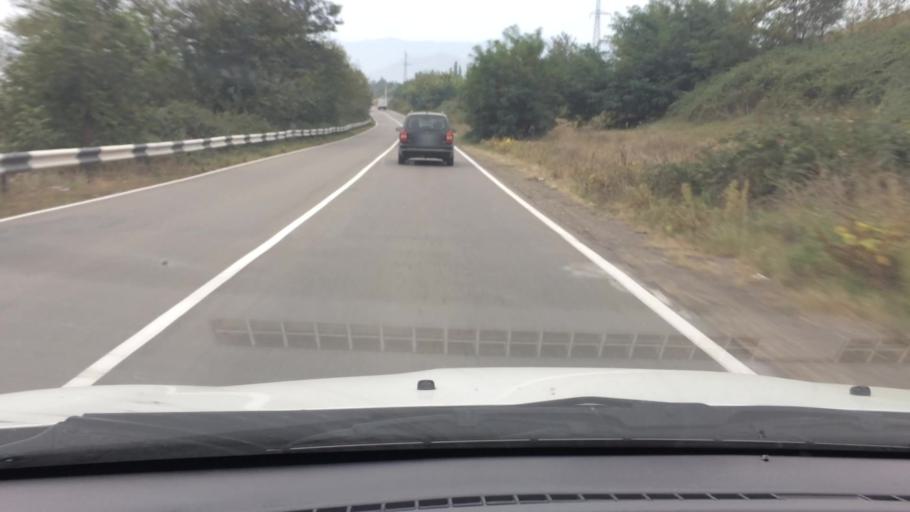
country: AM
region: Tavush
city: Bagratashen
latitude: 41.2713
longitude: 44.7907
